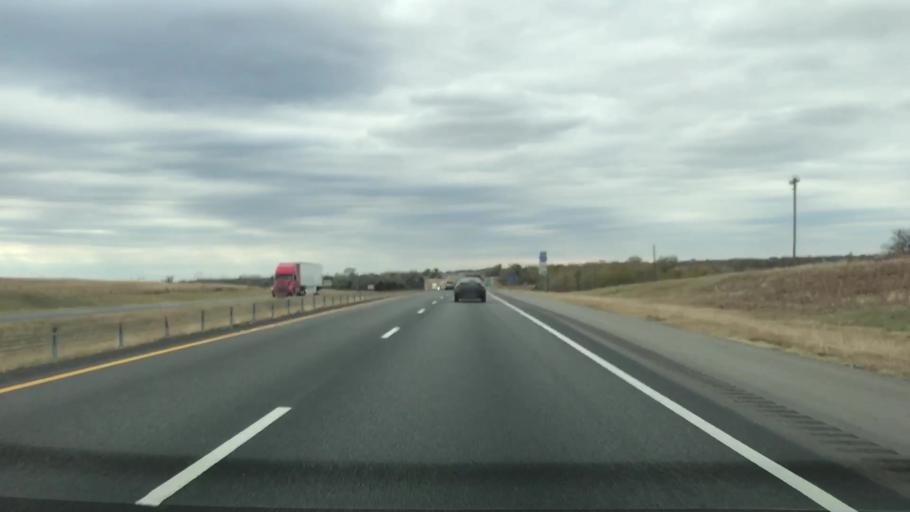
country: US
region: Oklahoma
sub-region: Beckham County
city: Elk City
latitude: 35.3858
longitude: -99.4781
